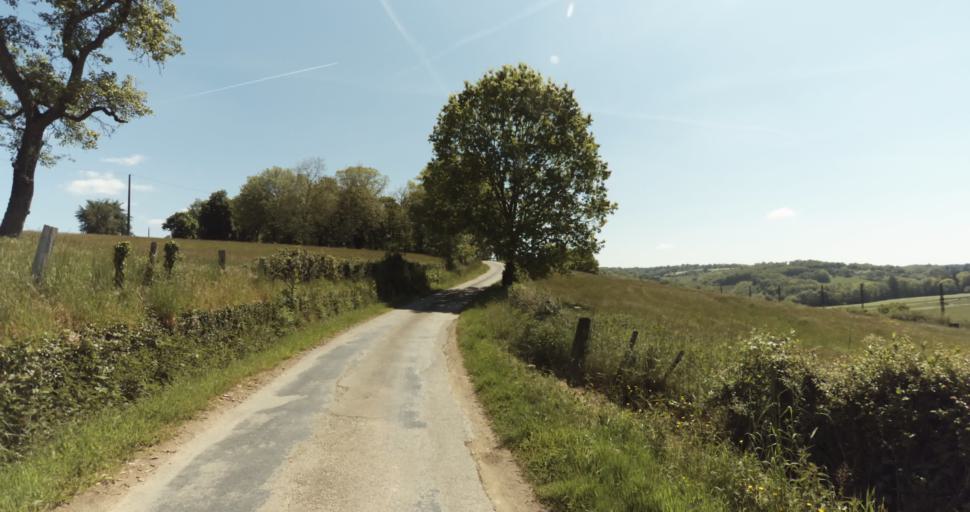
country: FR
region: Limousin
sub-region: Departement de la Haute-Vienne
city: Le Vigen
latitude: 45.7517
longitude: 1.2974
